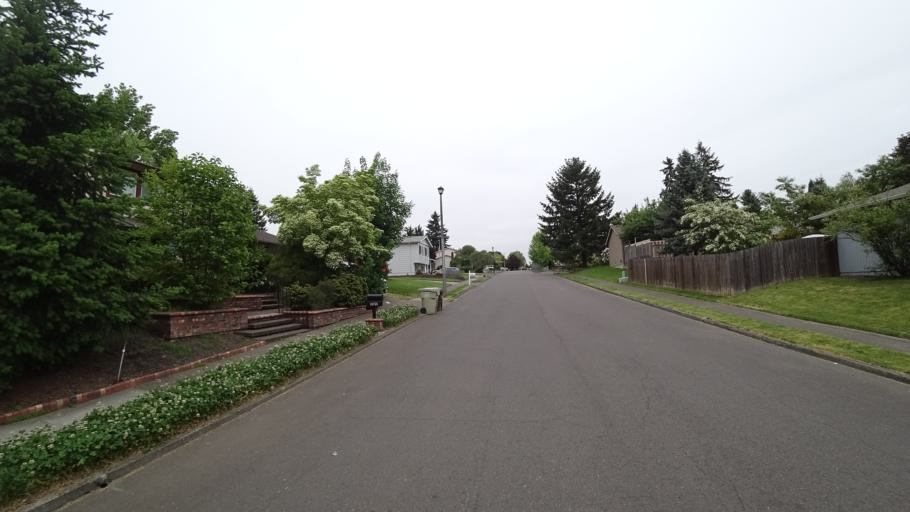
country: US
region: Oregon
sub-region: Washington County
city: Bethany
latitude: 45.5445
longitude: -122.8641
